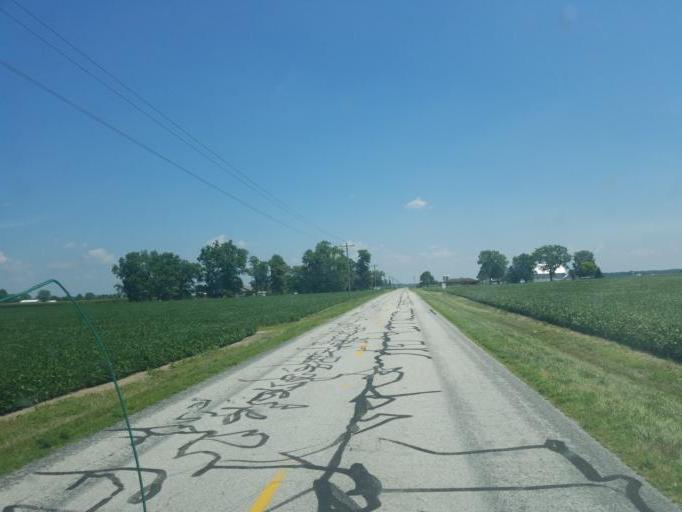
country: US
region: Ohio
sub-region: Auglaize County
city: Wapakoneta
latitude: 40.5403
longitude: -84.2855
